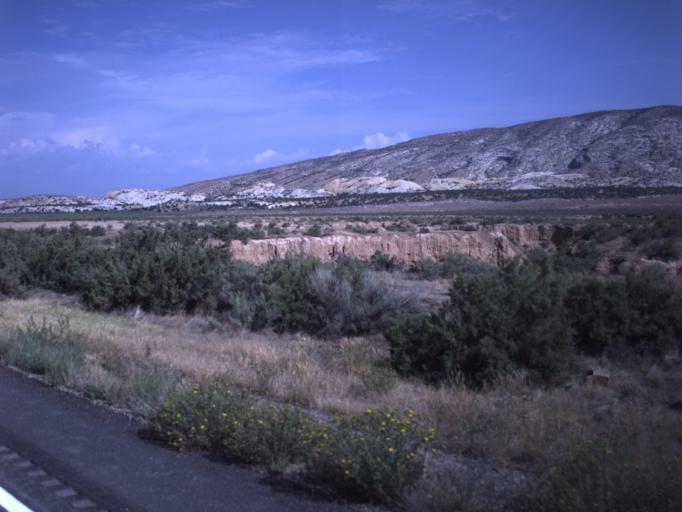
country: US
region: Utah
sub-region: Uintah County
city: Naples
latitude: 40.3092
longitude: -109.2181
